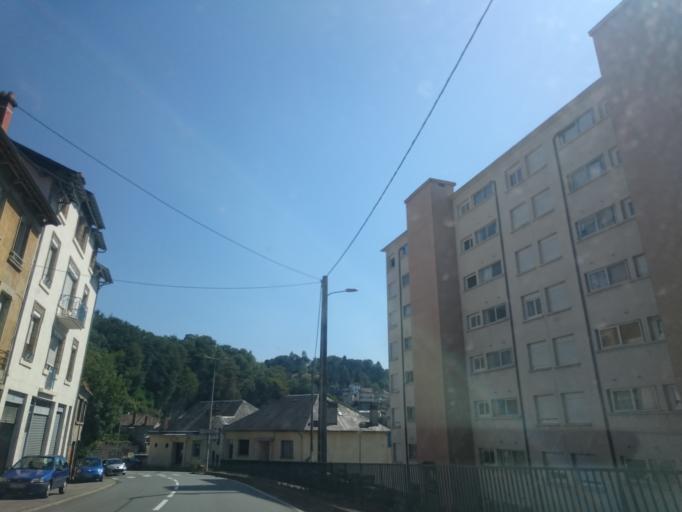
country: FR
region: Limousin
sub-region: Departement de la Correze
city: Tulle
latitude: 45.2733
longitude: 1.7767
